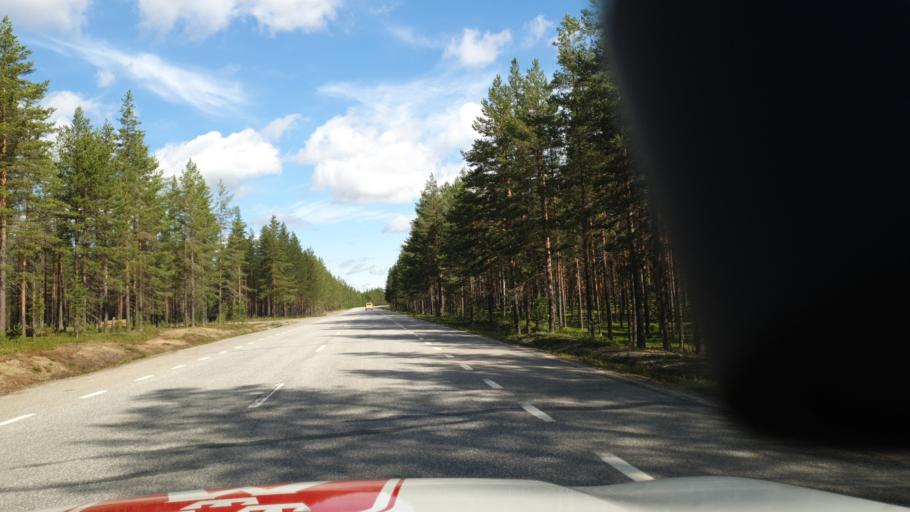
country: SE
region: Vaesterbotten
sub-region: Norsjo Kommun
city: Norsjoe
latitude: 64.5835
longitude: 19.3000
